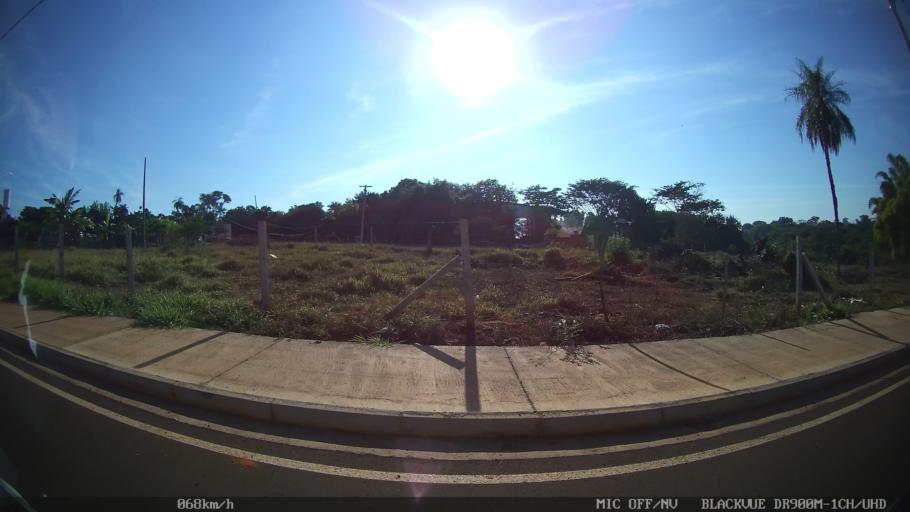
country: BR
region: Sao Paulo
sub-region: Sao Jose Do Rio Preto
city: Sao Jose do Rio Preto
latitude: -20.7737
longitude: -49.3491
